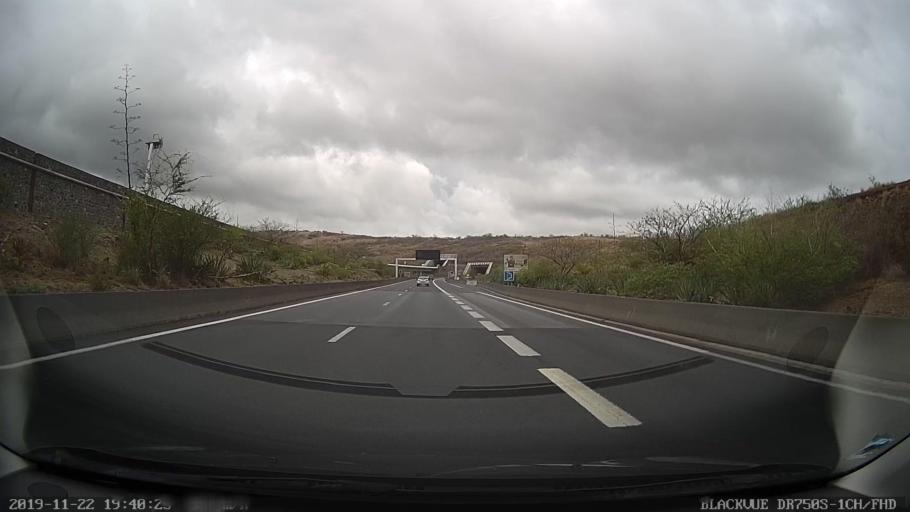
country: RE
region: Reunion
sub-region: Reunion
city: Saint-Paul
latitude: -21.0247
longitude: 55.2556
